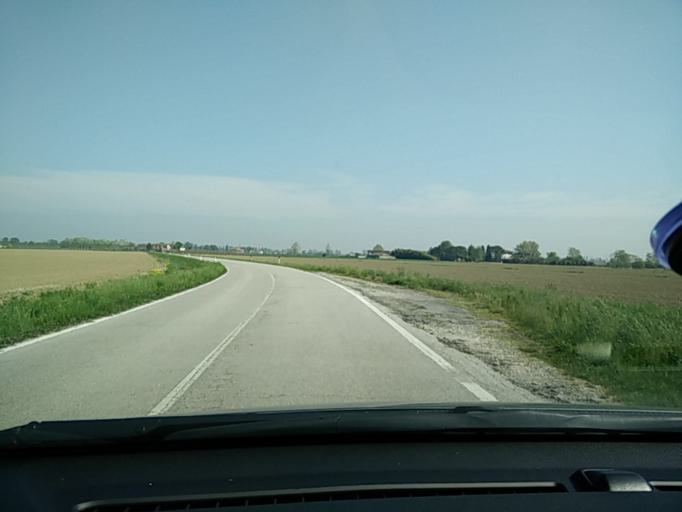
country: IT
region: Veneto
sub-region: Provincia di Treviso
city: Zenson di Piave
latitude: 45.6710
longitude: 12.4626
